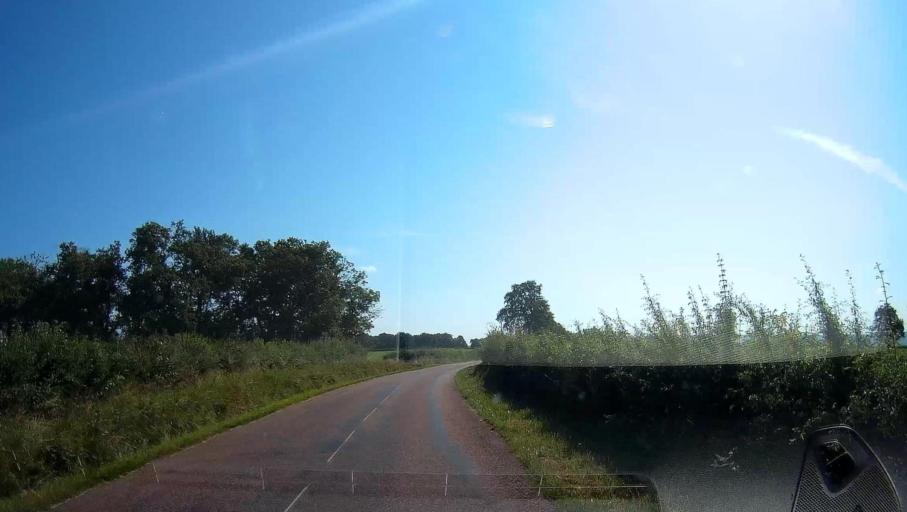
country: FR
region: Bourgogne
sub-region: Departement de Saone-et-Loire
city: Couches
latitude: 46.8843
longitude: 4.5418
